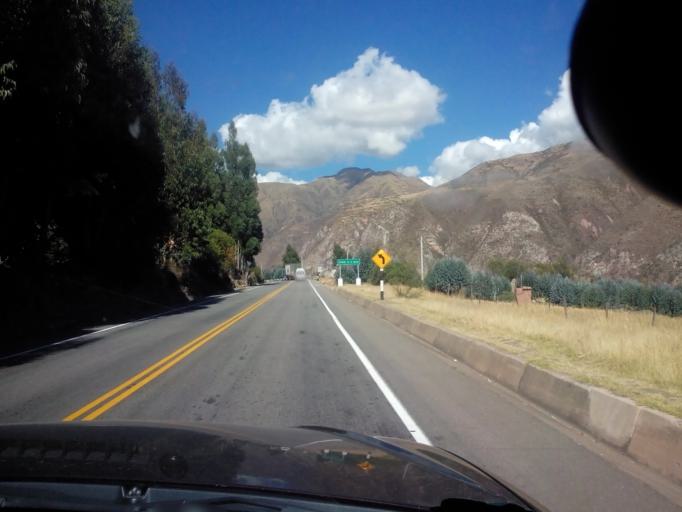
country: PE
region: Cusco
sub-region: Provincia de Quispicanchis
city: Urcos
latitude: -13.7057
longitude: -71.5967
